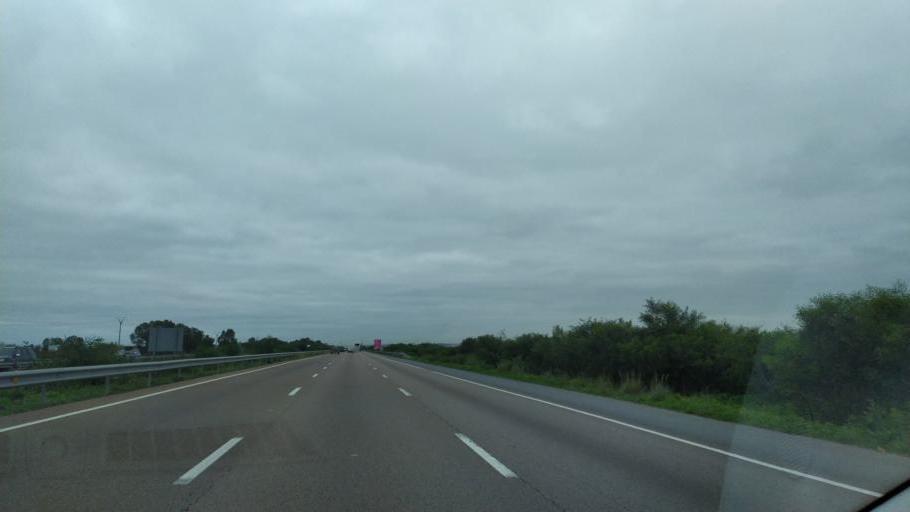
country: MA
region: Chaouia-Ouardigha
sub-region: Benslimane
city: Bouznika
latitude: 33.7851
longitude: -7.2190
